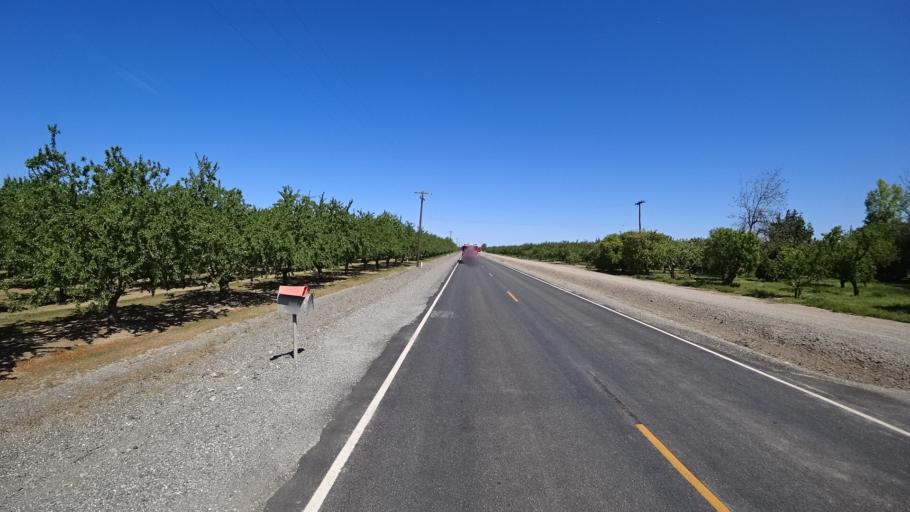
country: US
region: California
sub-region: Glenn County
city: Orland
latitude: 39.6711
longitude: -122.1406
